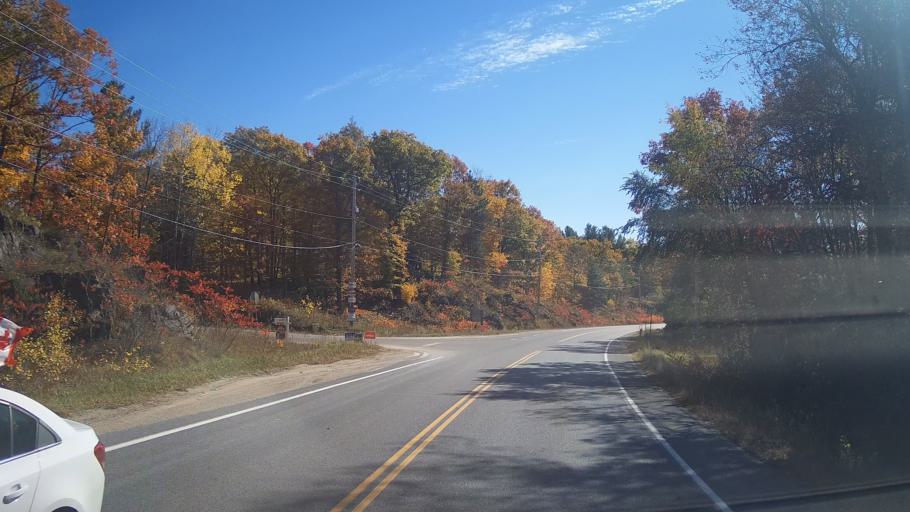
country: CA
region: Ontario
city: Perth
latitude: 44.6761
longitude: -76.6706
